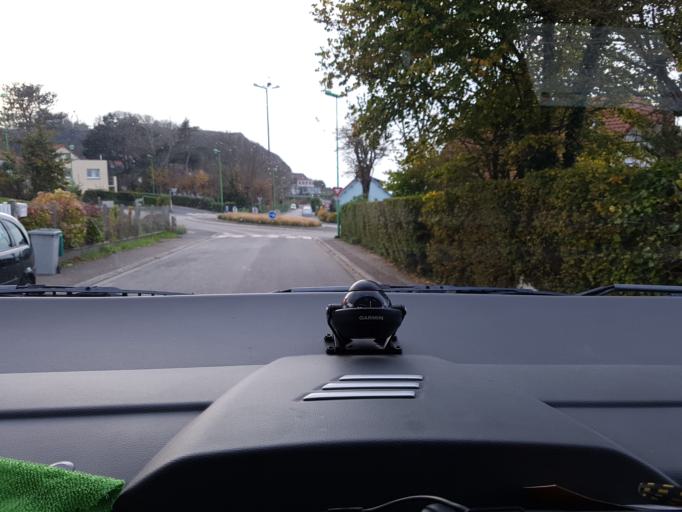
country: FR
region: Haute-Normandie
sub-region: Departement de la Seine-Maritime
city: Berneval-le-Grand
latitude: 49.9672
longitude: 1.1979
